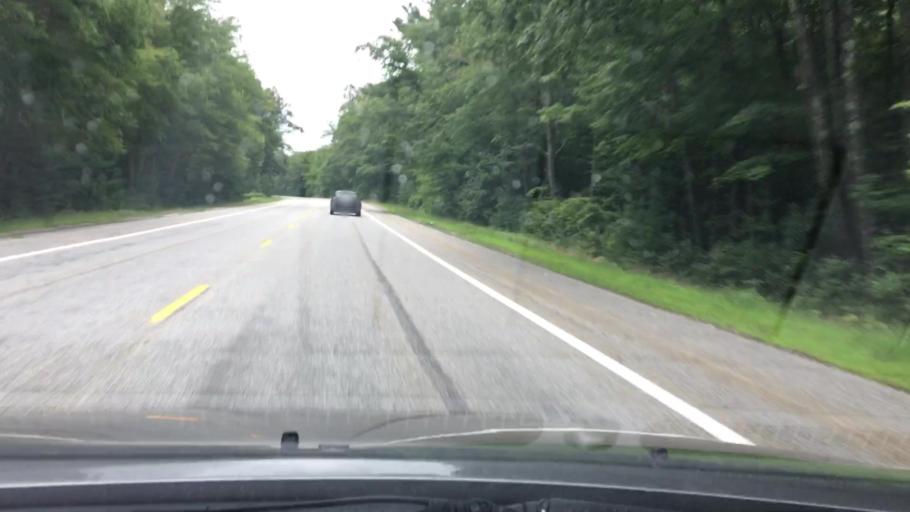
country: US
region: Rhode Island
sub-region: Providence County
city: Cumberland
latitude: 42.0102
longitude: -71.4407
